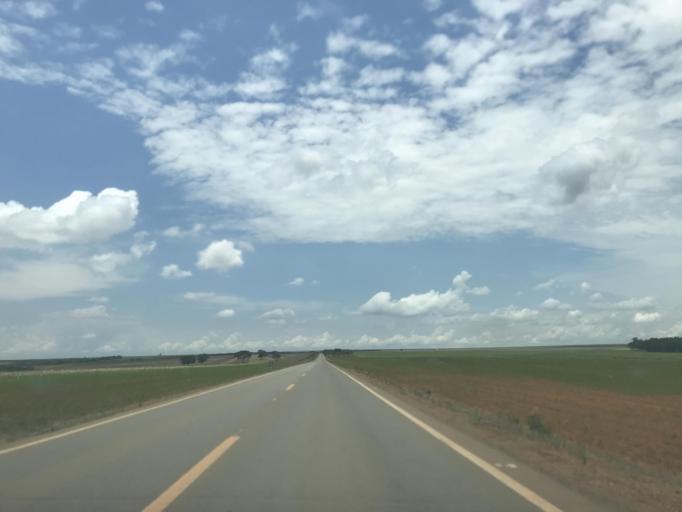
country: BR
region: Goias
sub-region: Luziania
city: Luziania
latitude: -16.5003
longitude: -48.2093
